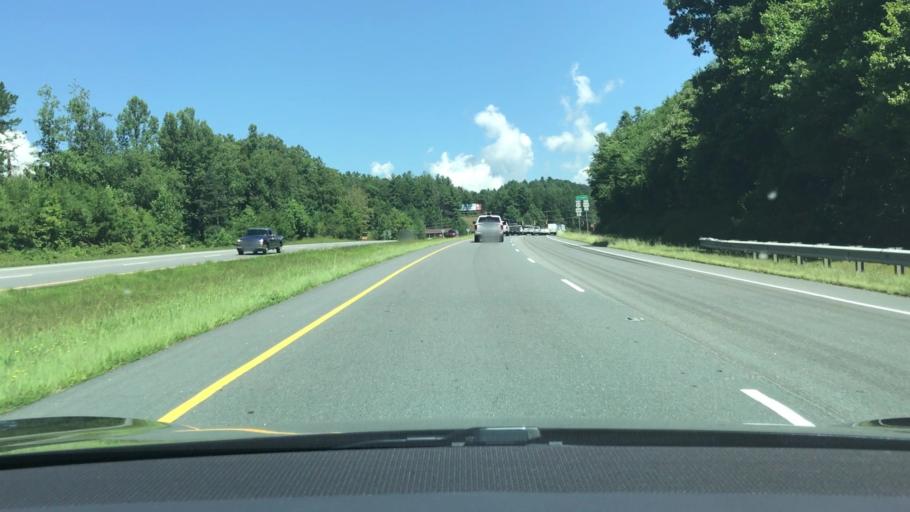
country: US
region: North Carolina
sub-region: Macon County
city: Franklin
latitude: 35.1912
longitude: -83.3609
